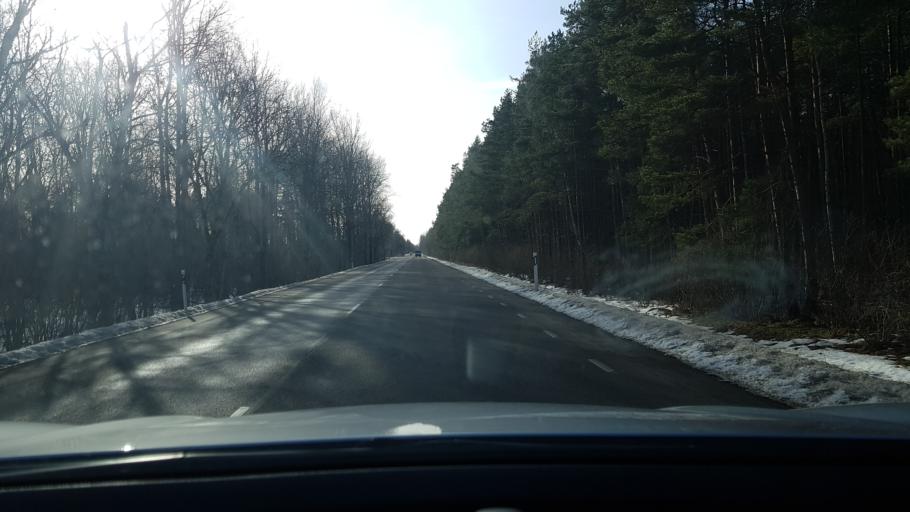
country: EE
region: Saare
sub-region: Orissaare vald
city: Orissaare
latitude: 58.5522
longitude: 23.0627
